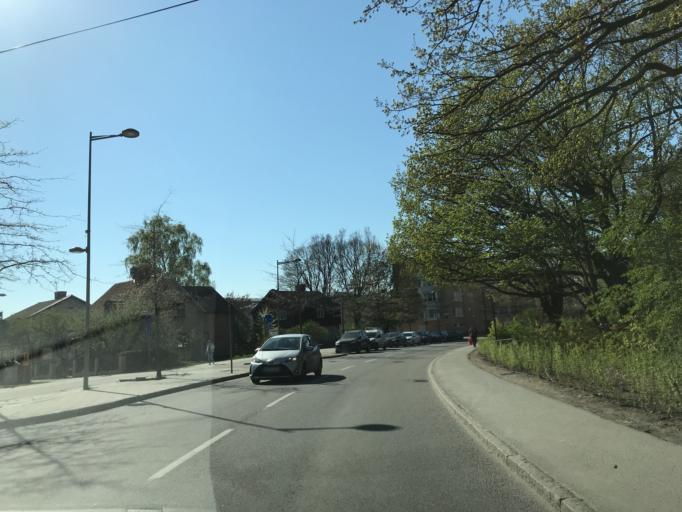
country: SE
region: Stockholm
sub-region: Stockholms Kommun
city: Arsta
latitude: 59.2791
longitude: 18.0080
